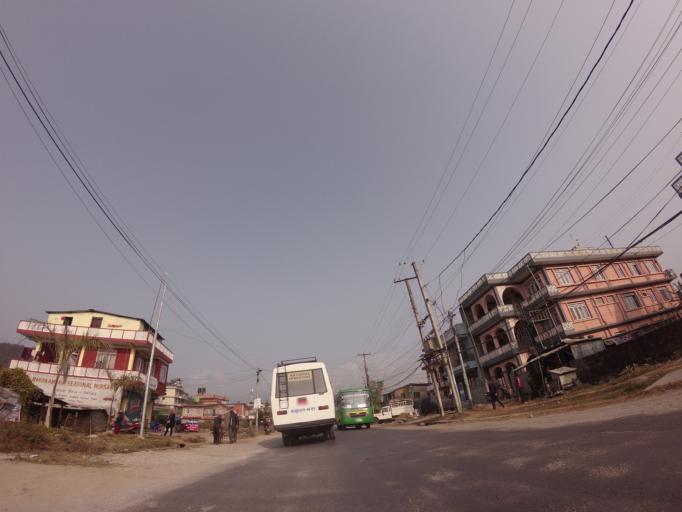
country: NP
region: Western Region
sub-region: Gandaki Zone
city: Pokhara
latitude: 28.1938
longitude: 83.9708
